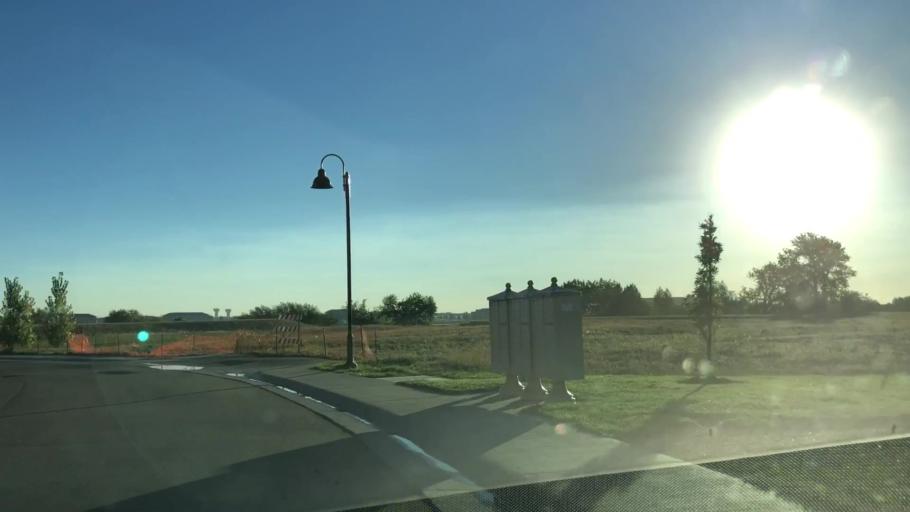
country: US
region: Colorado
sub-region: Larimer County
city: Loveland
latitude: 40.4148
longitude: -105.0148
